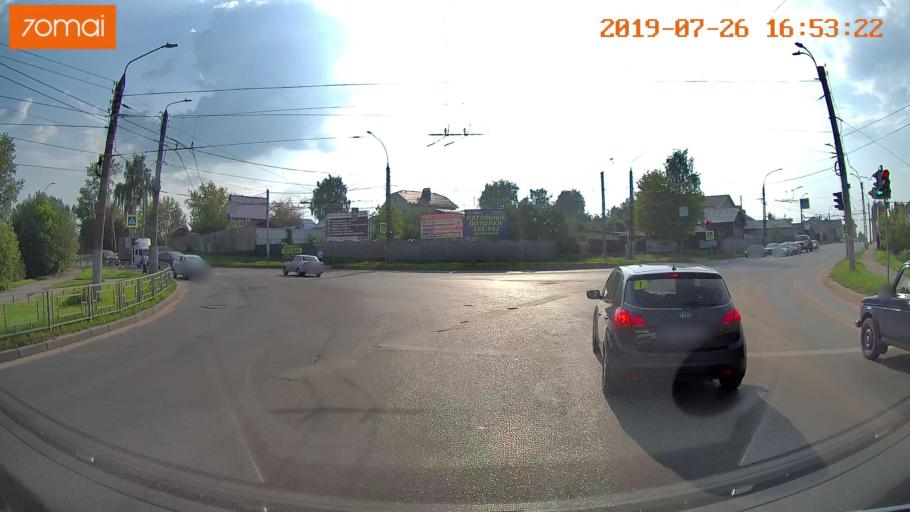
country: RU
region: Ivanovo
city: Bogorodskoye
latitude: 57.0166
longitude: 41.0030
